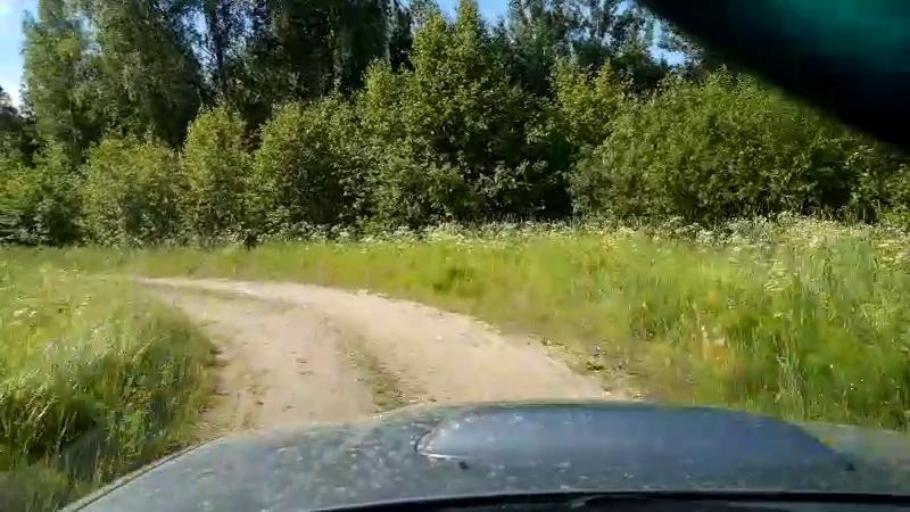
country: EE
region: Paernumaa
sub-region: Sindi linn
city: Sindi
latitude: 58.5036
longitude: 24.6416
